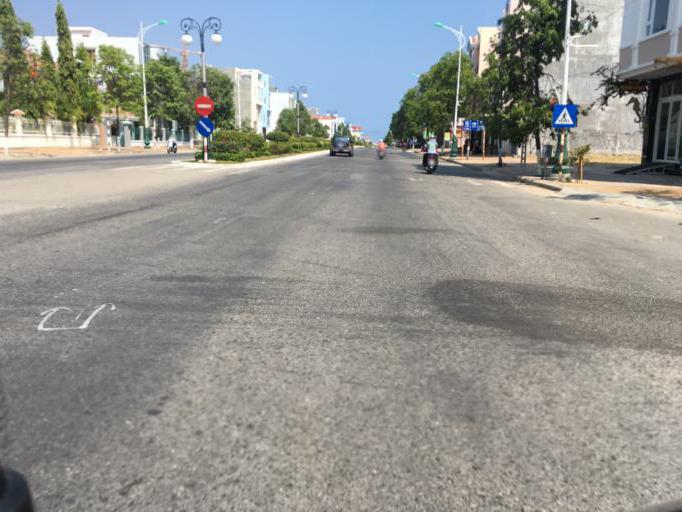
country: VN
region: Ninh Thuan
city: Phan Rang-Thap Cham
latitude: 11.5640
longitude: 109.0110
